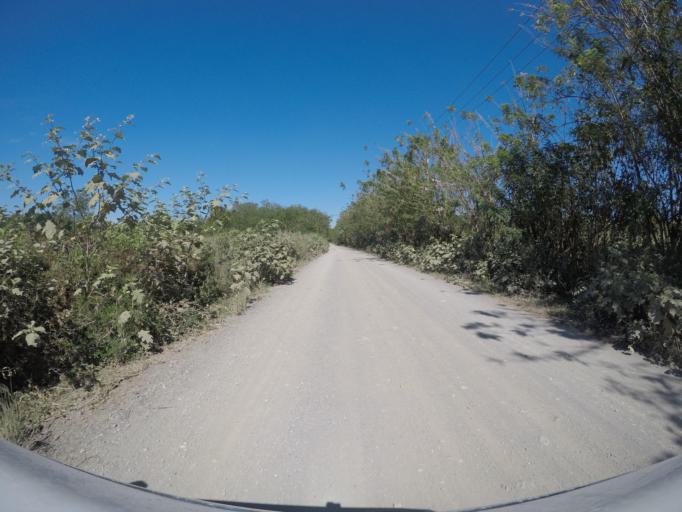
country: TL
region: Viqueque
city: Viqueque
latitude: -8.9734
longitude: 126.0679
